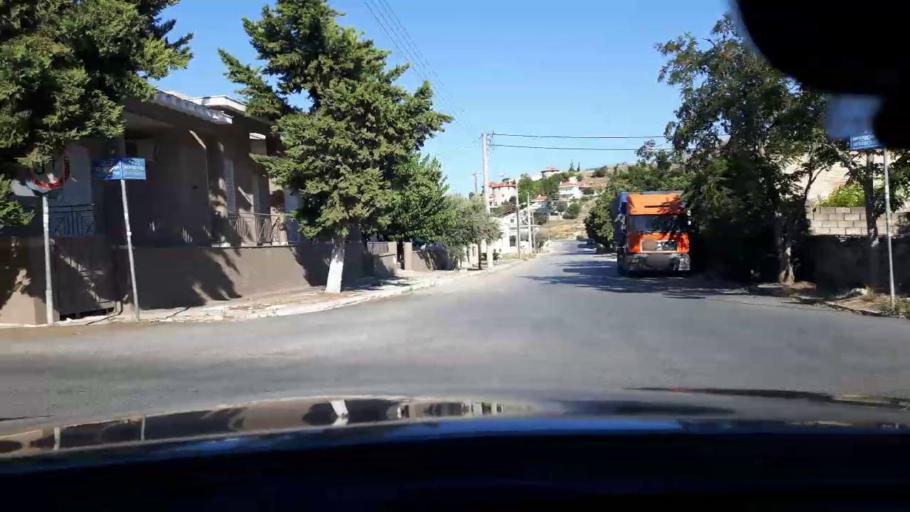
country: GR
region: Attica
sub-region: Nomarchia Anatolikis Attikis
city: Markopoulo
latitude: 37.8804
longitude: 23.9354
